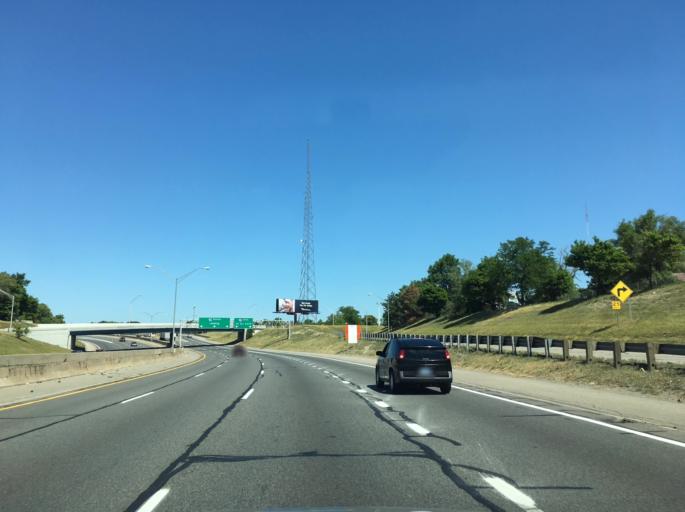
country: US
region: Michigan
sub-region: Wayne County
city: Highland Park
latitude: 42.3819
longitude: -83.1472
